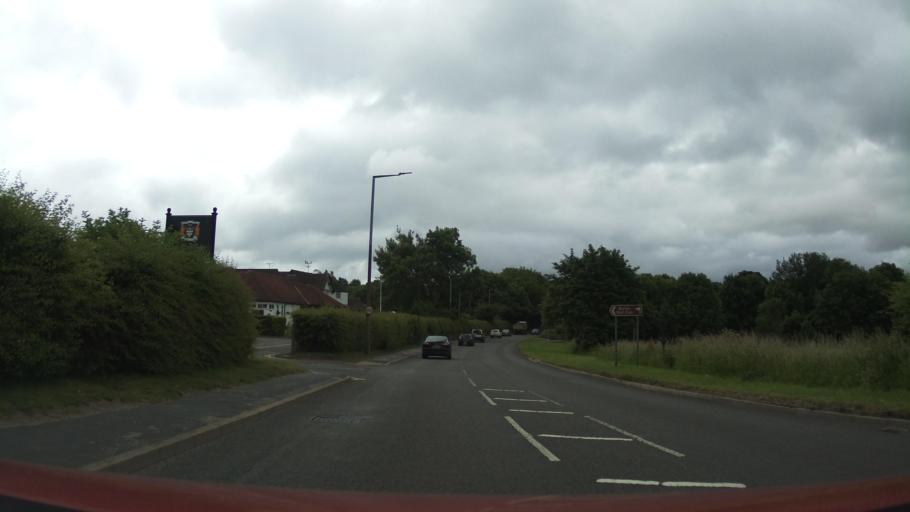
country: GB
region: England
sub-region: Derbyshire
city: Swadlincote
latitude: 52.7990
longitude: -1.5858
